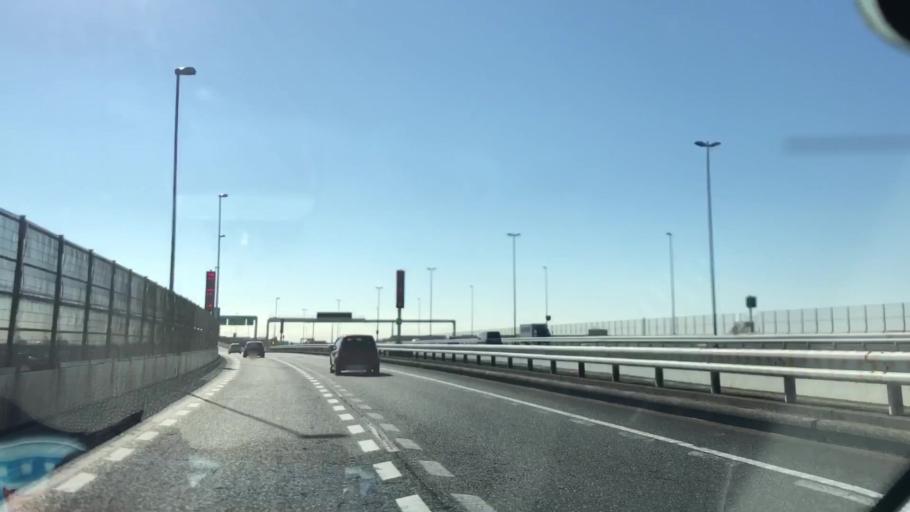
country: JP
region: Kanagawa
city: Yokohama
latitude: 35.4429
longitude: 139.6674
